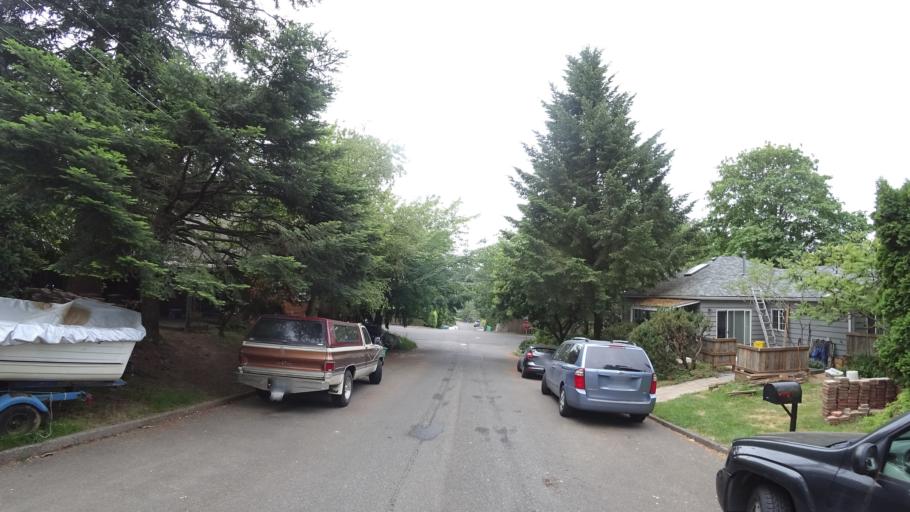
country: US
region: Oregon
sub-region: Clackamas County
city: Lake Oswego
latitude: 45.4632
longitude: -122.6866
